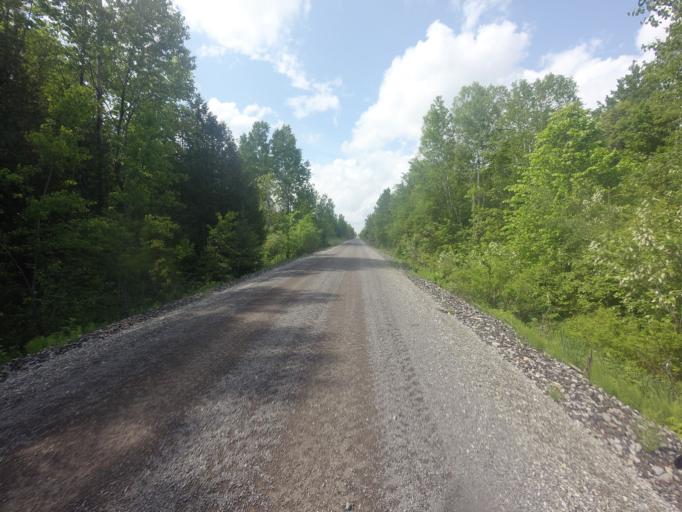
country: CA
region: Ontario
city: Carleton Place
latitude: 45.0486
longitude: -76.0883
